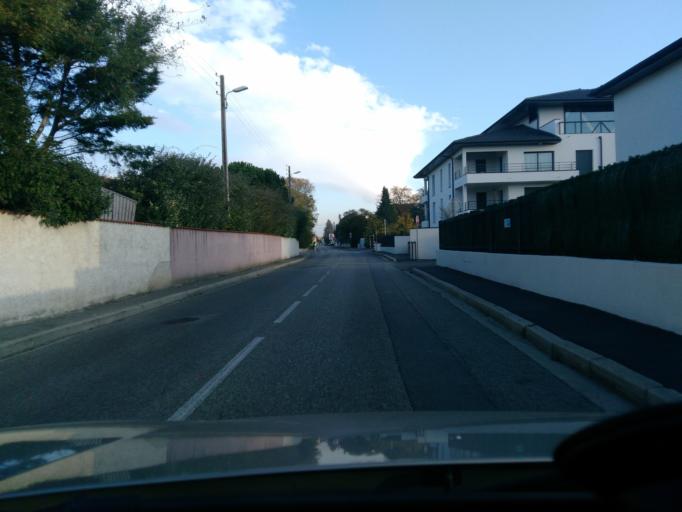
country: FR
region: Rhone-Alpes
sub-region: Departement de la Drome
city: Montelimar
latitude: 44.5409
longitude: 4.7440
